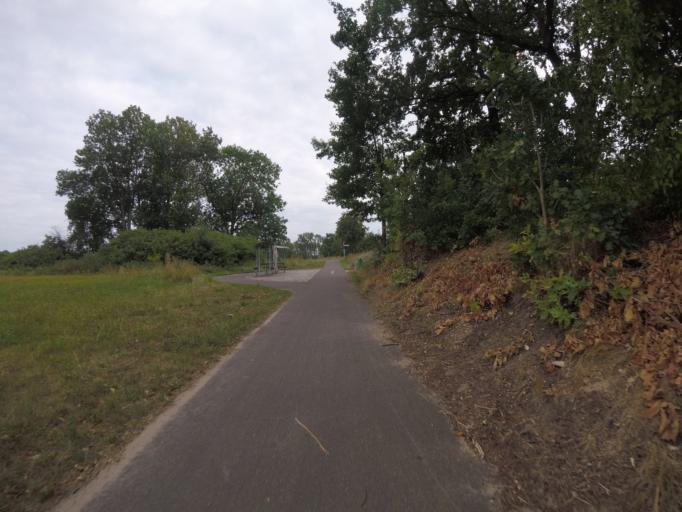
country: DE
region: Brandenburg
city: Liebenwalde
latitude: 52.8580
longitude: 13.3314
